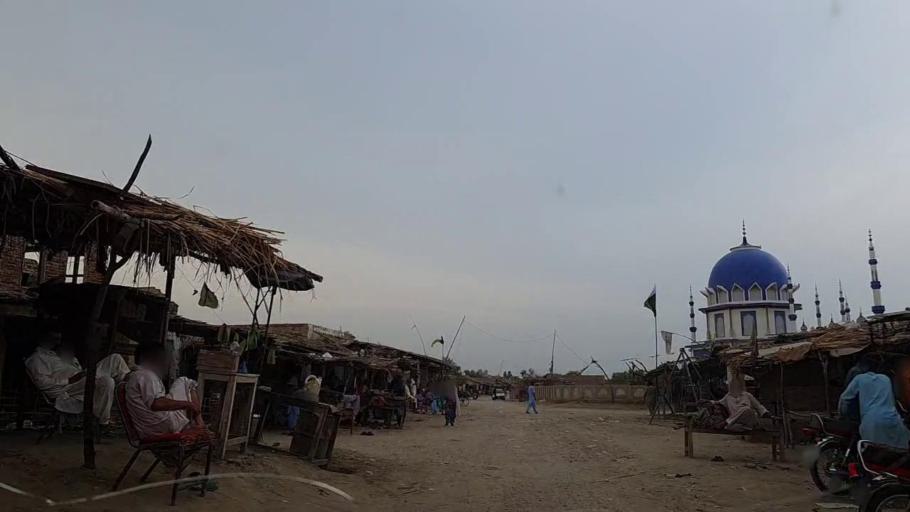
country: PK
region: Sindh
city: Mirpur Mathelo
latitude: 27.8982
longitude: 69.6565
